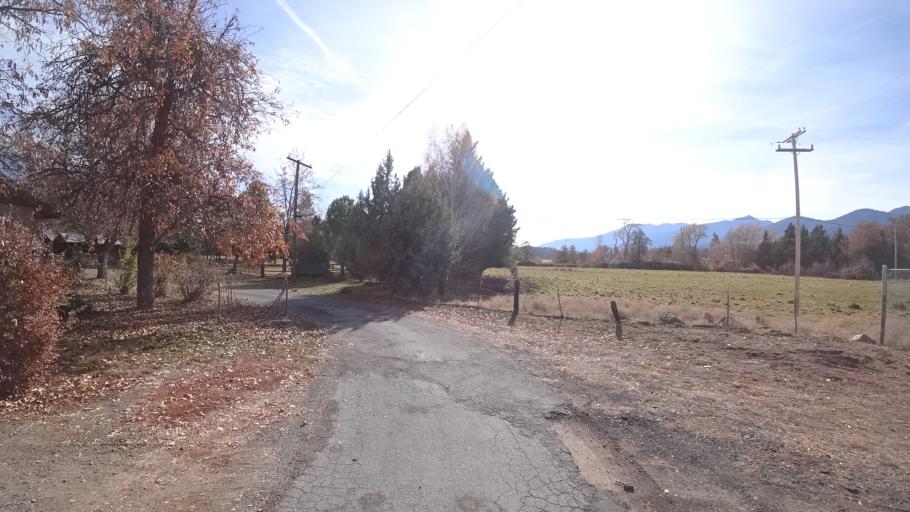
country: US
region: California
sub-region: Siskiyou County
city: Weed
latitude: 41.4566
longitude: -122.4307
